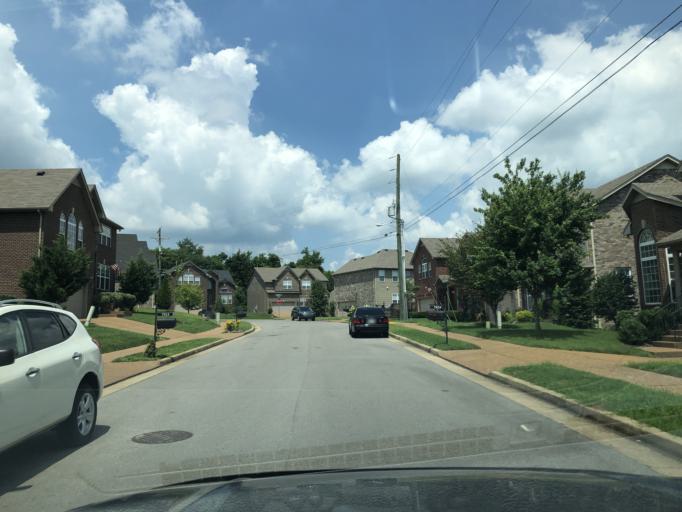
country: US
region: Tennessee
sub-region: Williamson County
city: Nolensville
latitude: 36.0157
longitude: -86.6920
